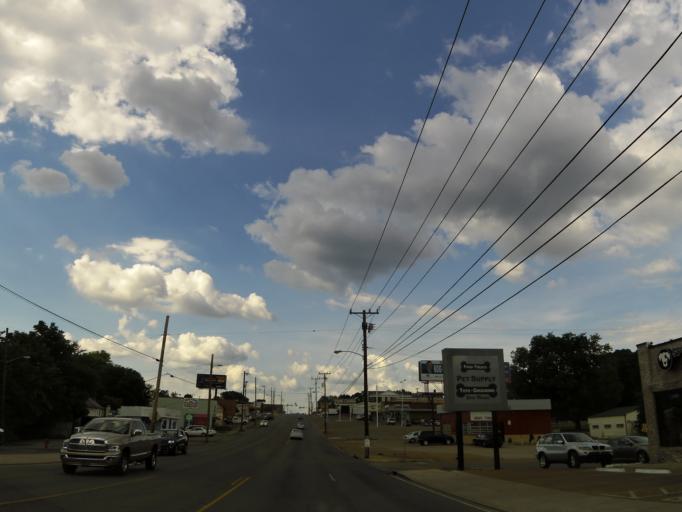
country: US
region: Tennessee
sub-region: Davidson County
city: Nashville
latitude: 36.1890
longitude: -86.7461
